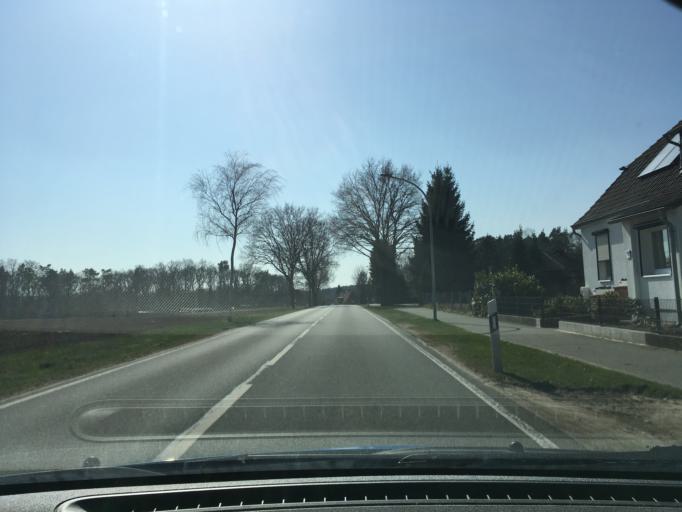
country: DE
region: Lower Saxony
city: Wriedel
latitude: 53.0246
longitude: 10.2855
